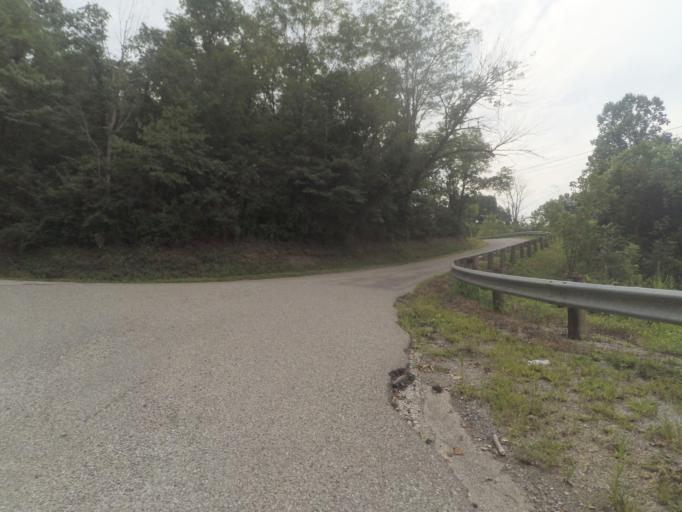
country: US
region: West Virginia
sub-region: Cabell County
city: Huntington
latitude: 38.4417
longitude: -82.4542
